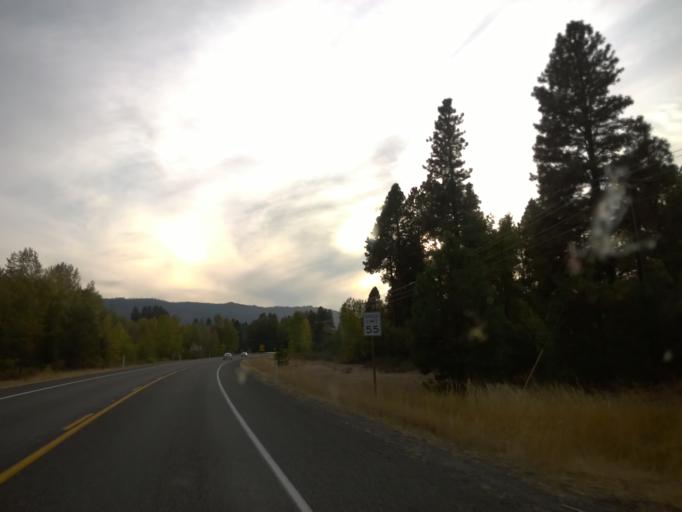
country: US
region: Washington
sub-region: Kittitas County
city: Cle Elum
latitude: 47.1760
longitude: -120.8473
